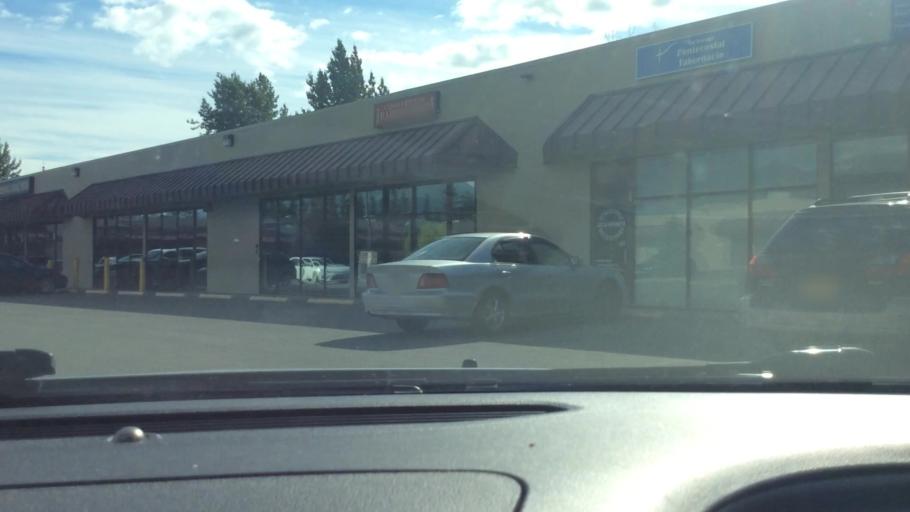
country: US
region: Alaska
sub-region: Anchorage Municipality
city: Anchorage
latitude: 61.2217
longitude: -149.7805
